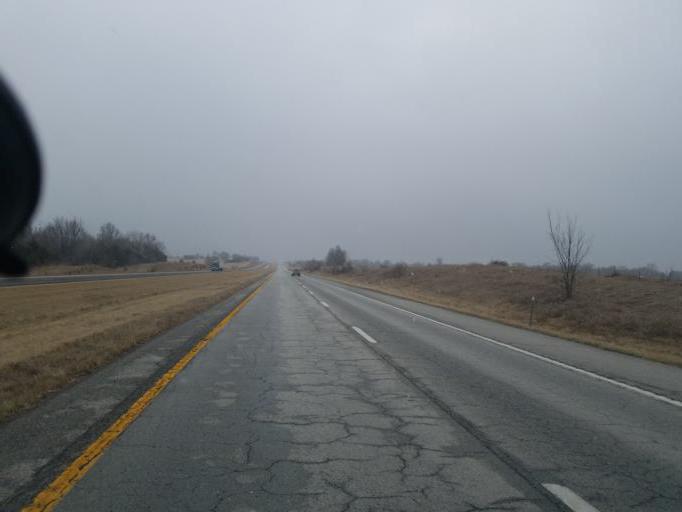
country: US
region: Missouri
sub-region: Macon County
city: La Plata
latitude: 39.9108
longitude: -92.4737
